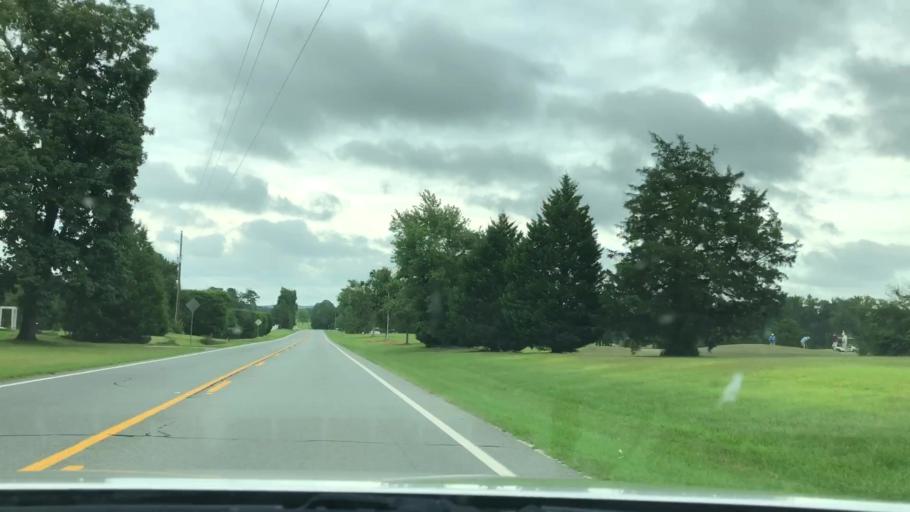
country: US
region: Georgia
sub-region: Pike County
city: Zebulon
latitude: 33.1110
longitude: -84.3928
